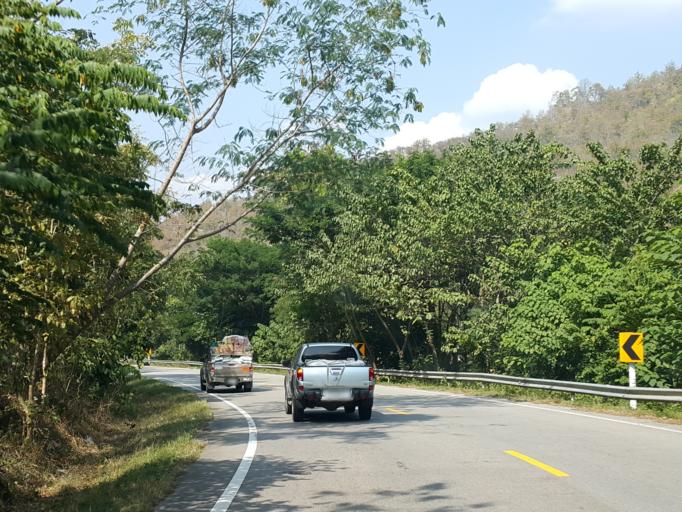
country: TH
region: Chiang Mai
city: Hot
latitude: 18.2323
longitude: 98.5558
